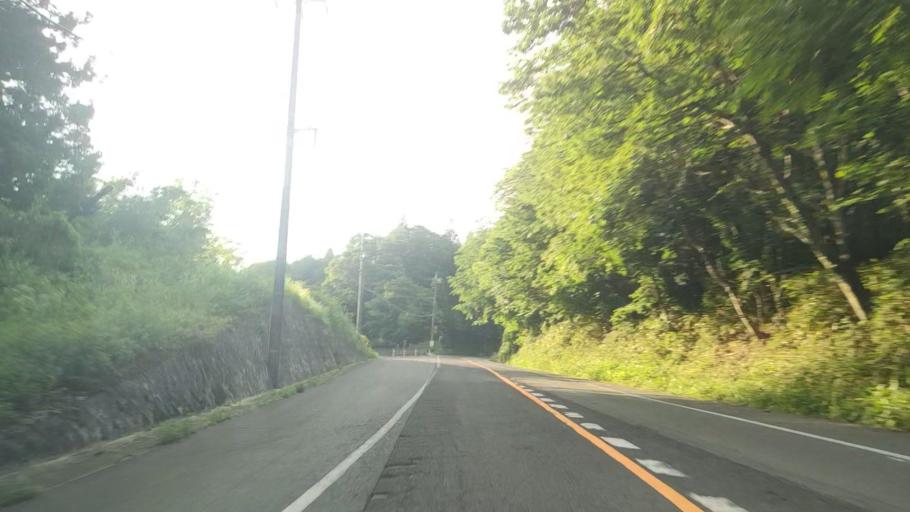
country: JP
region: Tottori
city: Kurayoshi
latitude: 35.2837
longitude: 133.6375
